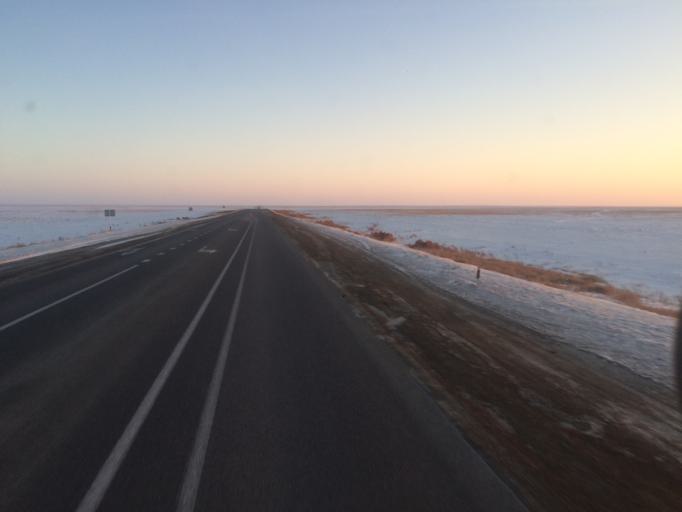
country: KZ
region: Qyzylorda
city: Sekseuil
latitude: 47.6031
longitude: 61.5011
